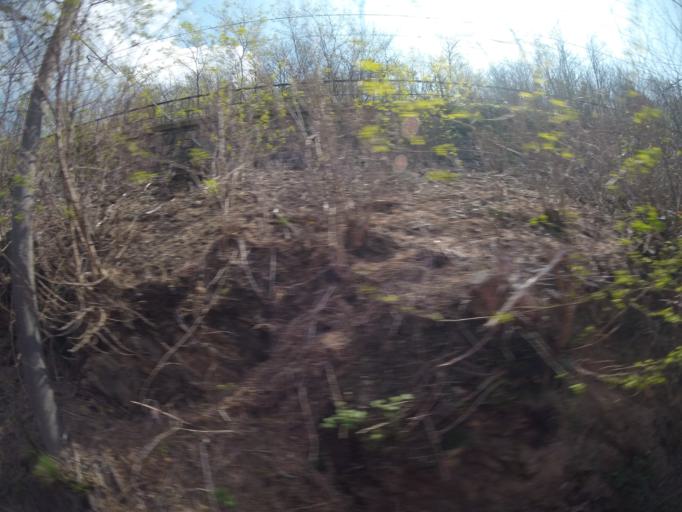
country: IT
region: Piedmont
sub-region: Provincia Verbano-Cusio-Ossola
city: Nonio
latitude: 45.8500
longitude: 8.4064
